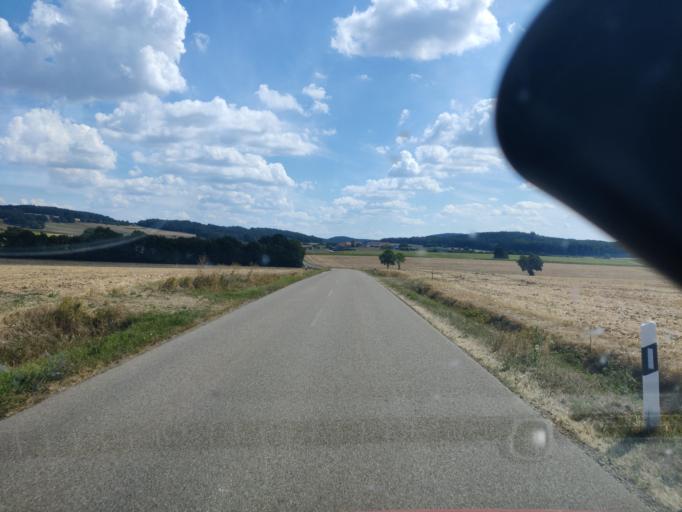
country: DE
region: Bavaria
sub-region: Regierungsbezirk Mittelfranken
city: Thalmassing
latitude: 49.1066
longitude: 11.2010
